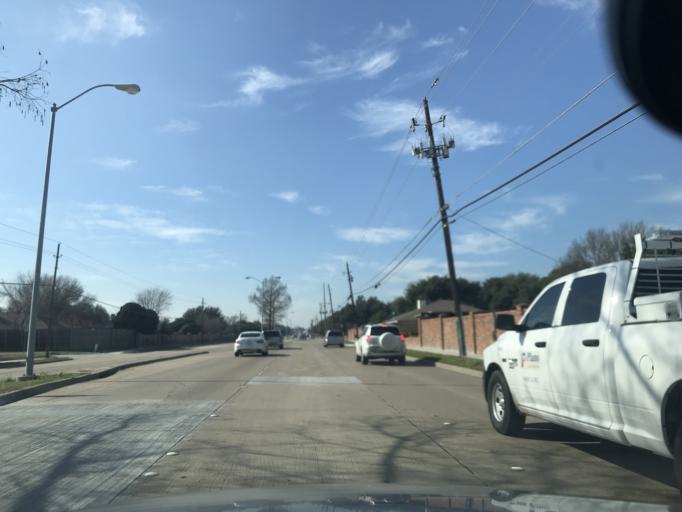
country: US
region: Texas
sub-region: Collin County
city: Plano
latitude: 33.0411
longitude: -96.7282
